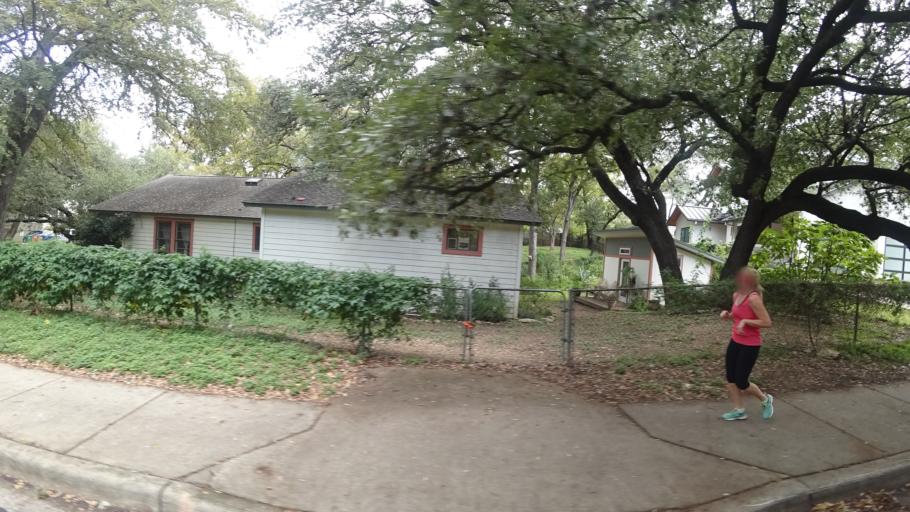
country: US
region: Texas
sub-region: Travis County
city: Austin
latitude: 30.2590
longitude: -97.7562
